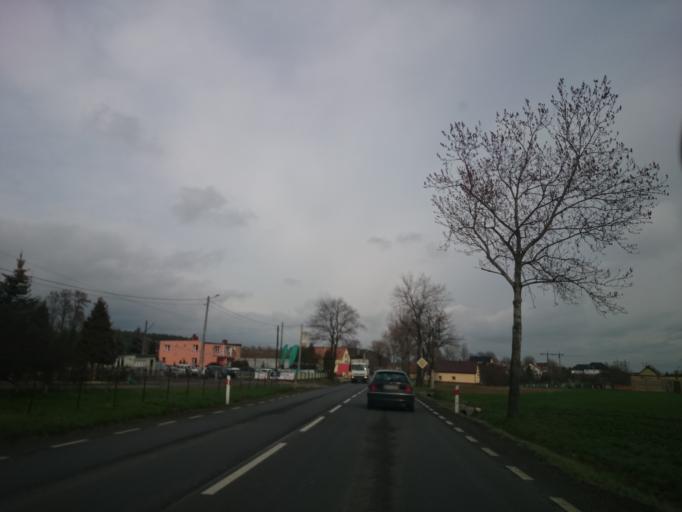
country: PL
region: Opole Voivodeship
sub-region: Powiat nyski
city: Otmuchow
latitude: 50.4684
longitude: 17.2115
